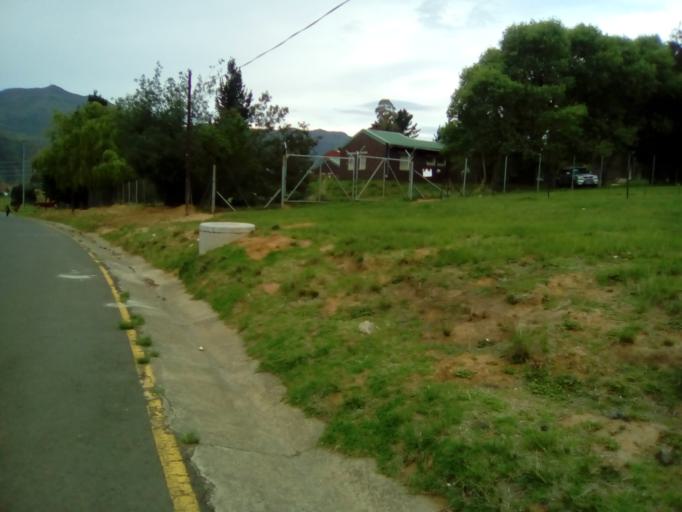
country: LS
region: Qacha's Nek
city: Qacha's Nek
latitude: -30.1127
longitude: 28.6810
